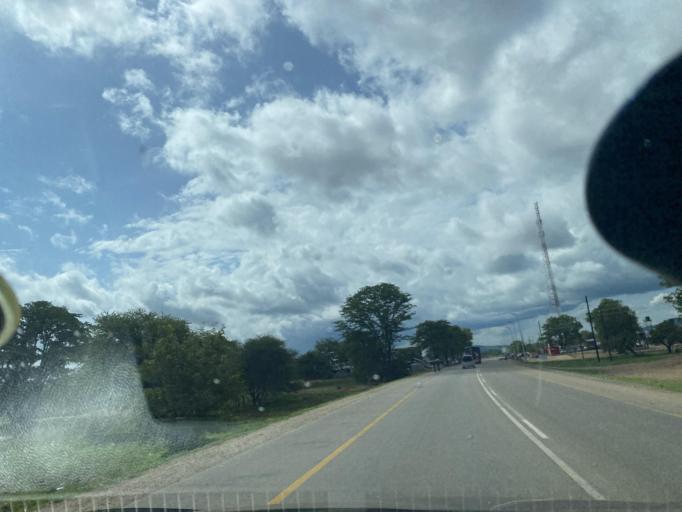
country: ZM
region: Lusaka
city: Kafue
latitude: -15.8526
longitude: 28.2518
